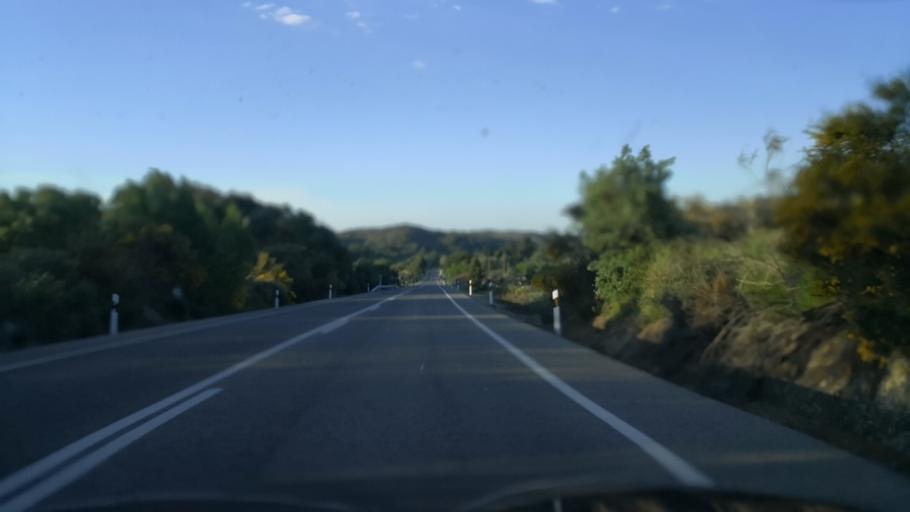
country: PT
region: Portalegre
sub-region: Portalegre
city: Sao Juliao
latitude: 39.3593
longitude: -7.2749
